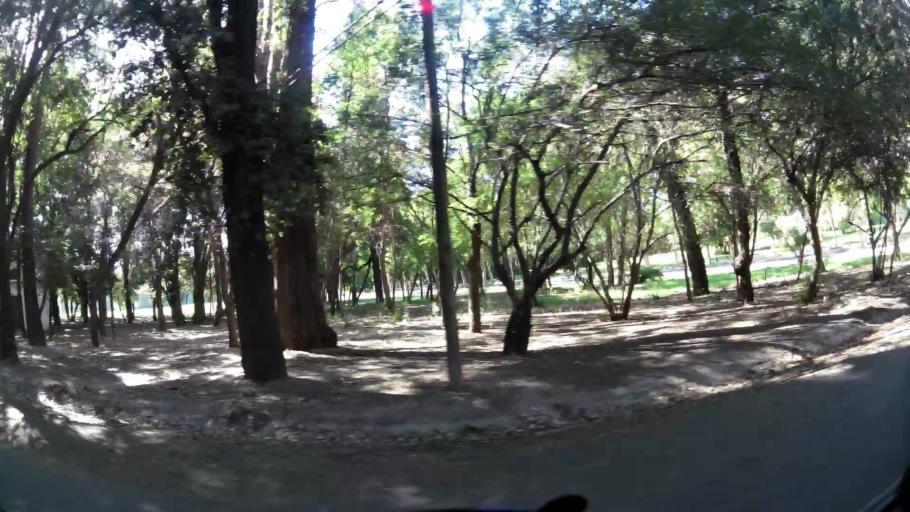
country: AR
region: Mendoza
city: Mendoza
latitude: -32.8878
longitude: -68.8699
